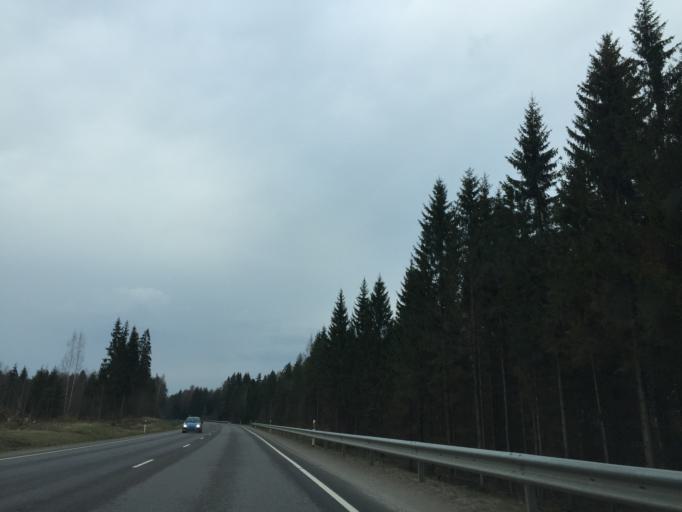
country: EE
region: Tartu
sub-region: UElenurme vald
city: Ulenurme
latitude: 58.0987
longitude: 26.7400
